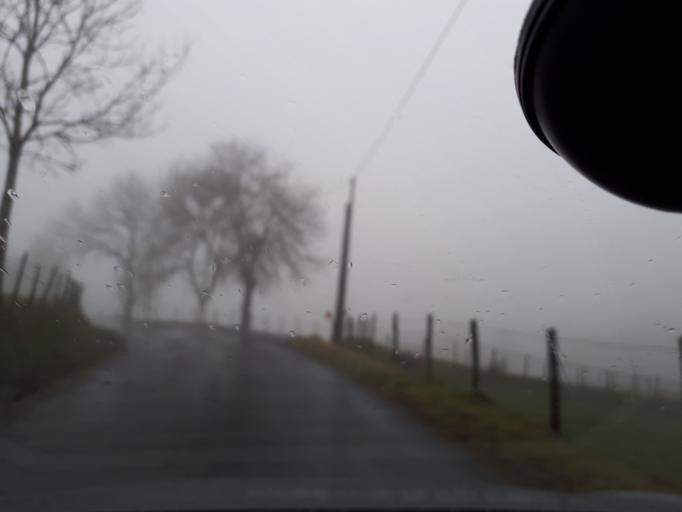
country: FR
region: Rhone-Alpes
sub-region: Departement du Rhone
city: Amplepuis
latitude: 45.9627
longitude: 4.3891
